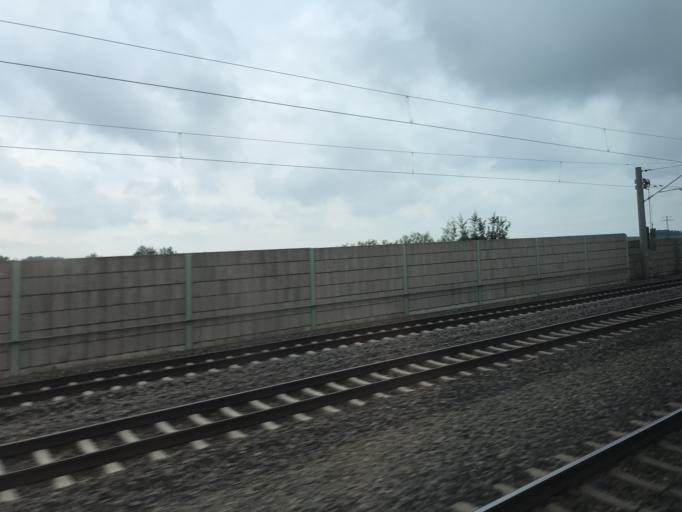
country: DE
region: Bavaria
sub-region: Upper Bavaria
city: Althegnenberg
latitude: 48.2385
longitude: 11.0580
